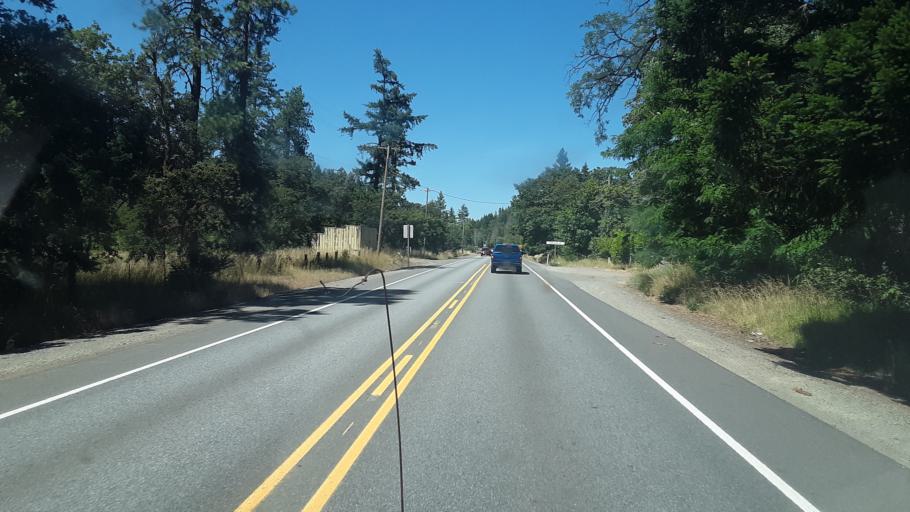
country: US
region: Oregon
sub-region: Josephine County
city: Cave Junction
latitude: 42.2844
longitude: -123.6142
